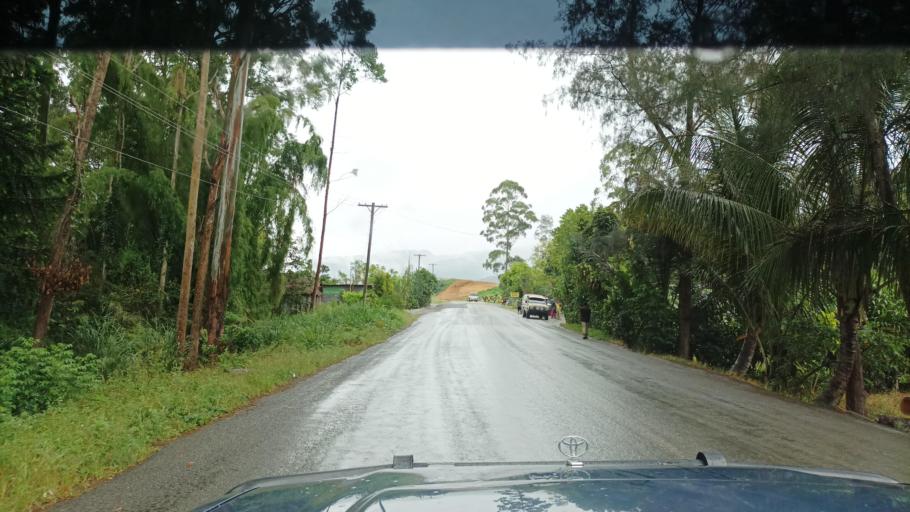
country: PG
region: Jiwaka
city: Minj
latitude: -5.8444
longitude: 144.6219
